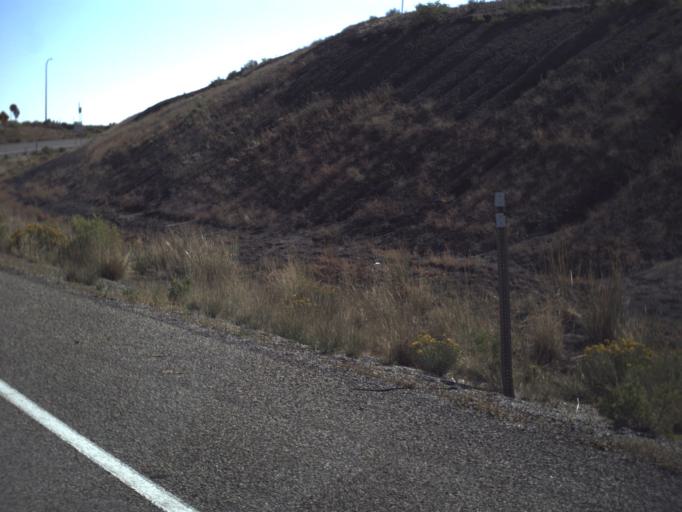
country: US
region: Utah
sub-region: Emery County
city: Castle Dale
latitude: 39.1748
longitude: -111.0490
